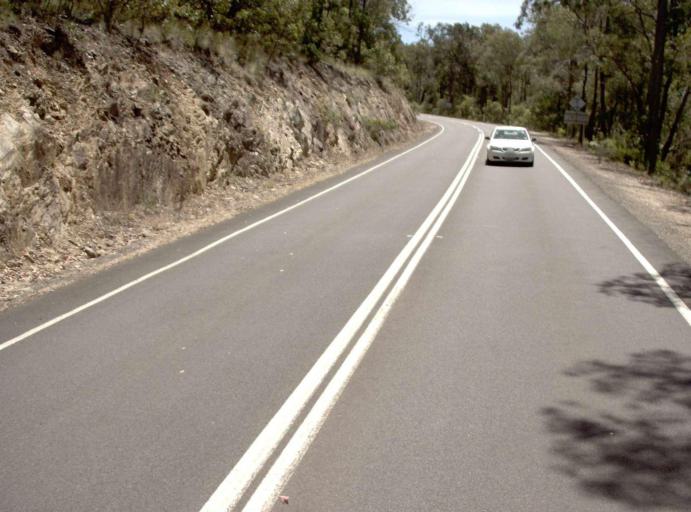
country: AU
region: Victoria
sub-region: East Gippsland
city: Lakes Entrance
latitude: -37.6163
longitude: 147.8829
